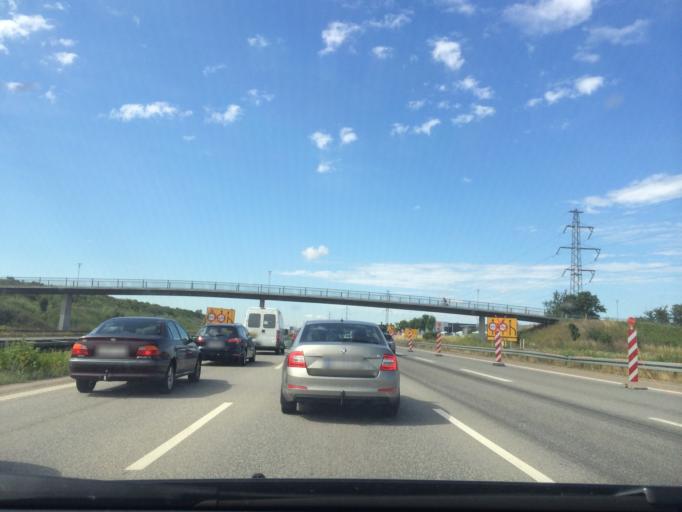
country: DK
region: Zealand
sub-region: Greve Kommune
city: Greve
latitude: 55.5903
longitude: 12.2710
